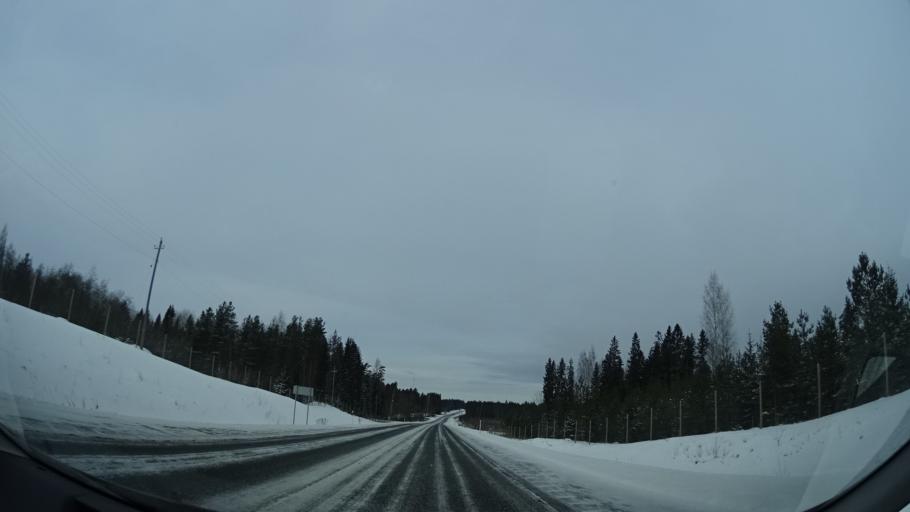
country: FI
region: Uusimaa
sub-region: Helsinki
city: Kaerkoelae
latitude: 60.6378
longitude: 23.8953
